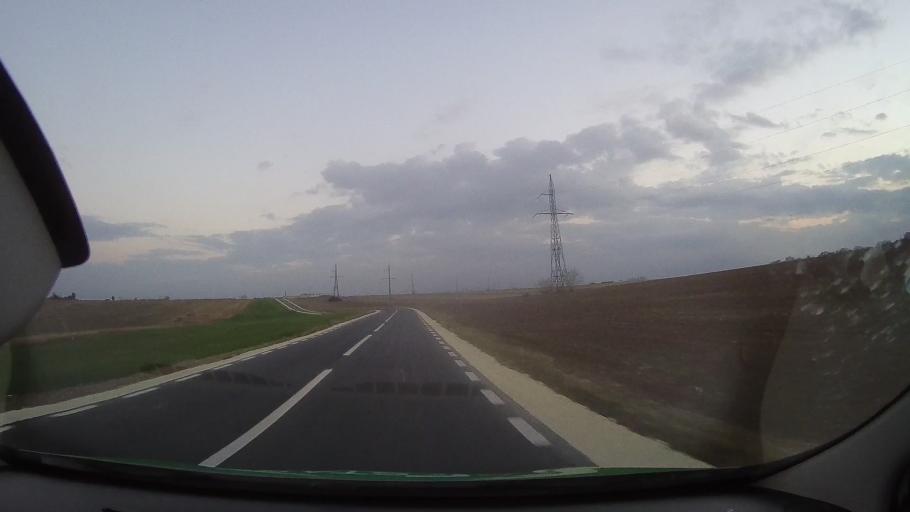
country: RO
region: Constanta
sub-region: Comuna Baneasa
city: Baneasa
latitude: 44.1068
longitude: 27.6711
